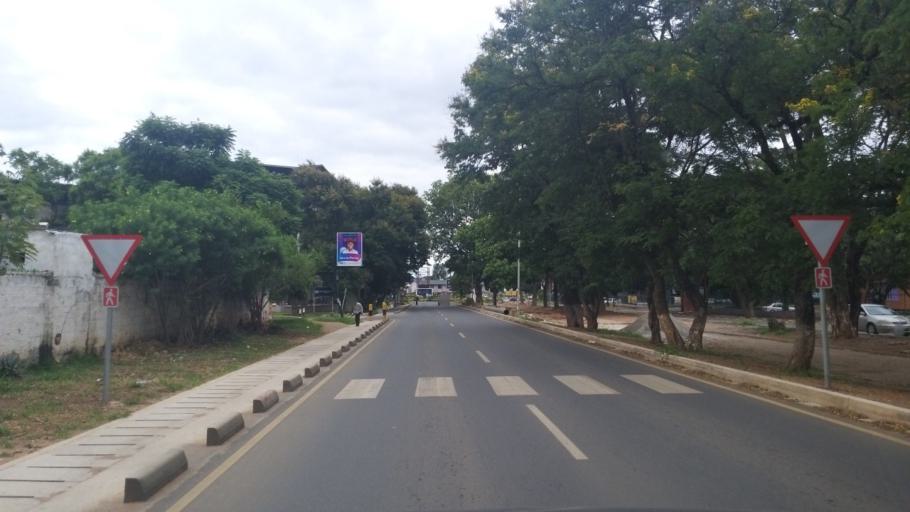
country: ZM
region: Lusaka
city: Lusaka
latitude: -15.4157
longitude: 28.3040
